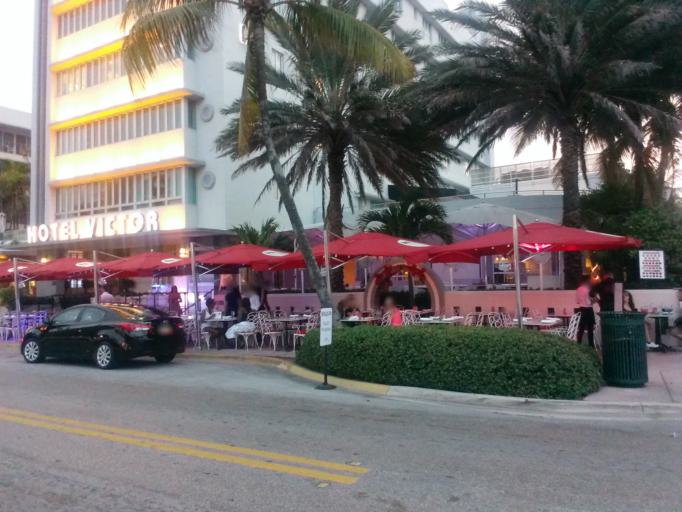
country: US
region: Florida
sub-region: Miami-Dade County
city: Miami Beach
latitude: 25.7826
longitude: -80.1301
